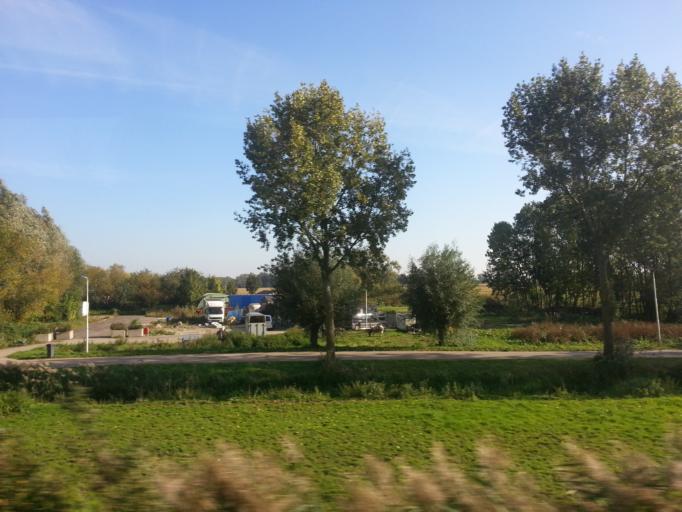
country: NL
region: Gelderland
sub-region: Gemeente Culemborg
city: Culemborg
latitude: 51.9404
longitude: 5.2331
